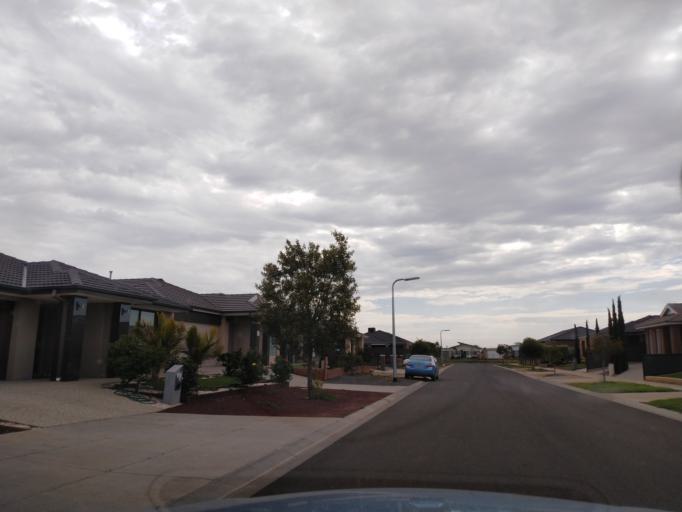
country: AU
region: Victoria
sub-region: Wyndham
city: Williams Landing
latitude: -37.8450
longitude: 144.7150
